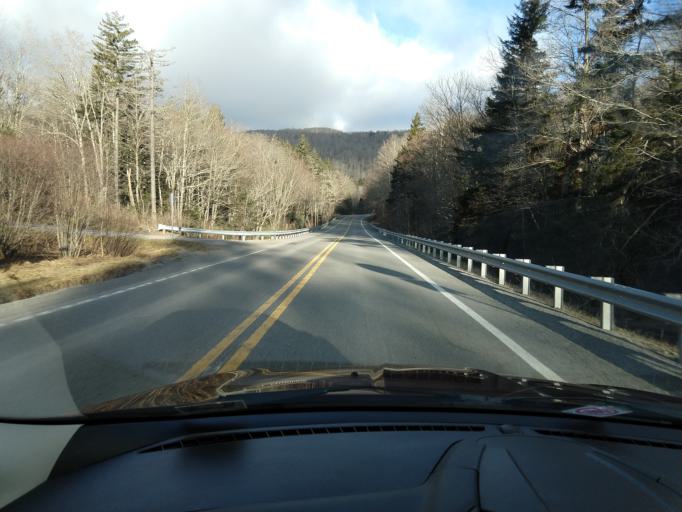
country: US
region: West Virginia
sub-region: Randolph County
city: Elkins
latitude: 38.6170
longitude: -79.8701
